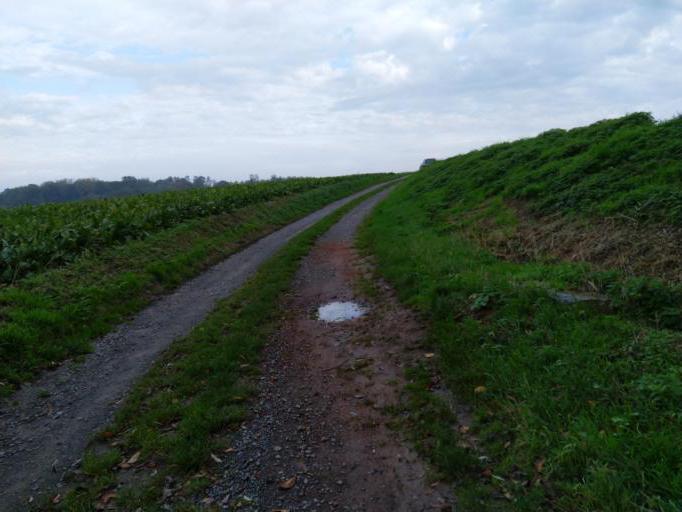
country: BE
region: Wallonia
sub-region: Province du Hainaut
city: Brugelette
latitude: 50.6142
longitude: 3.8729
